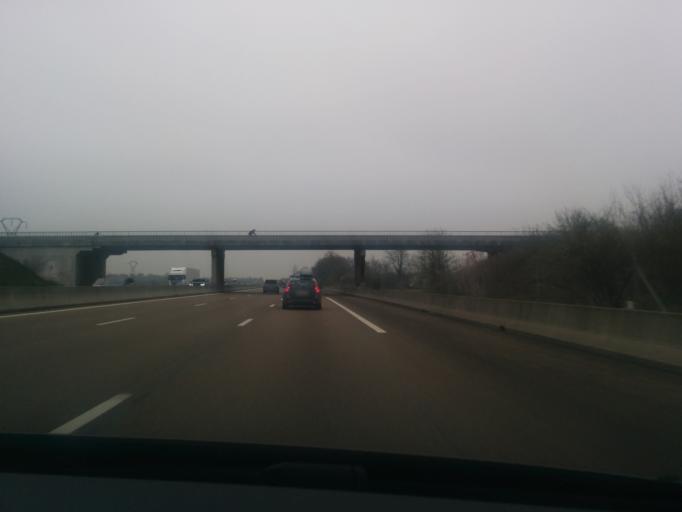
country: FR
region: Bourgogne
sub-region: Departement de la Cote-d'Or
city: Couternon
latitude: 47.3097
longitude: 5.1733
